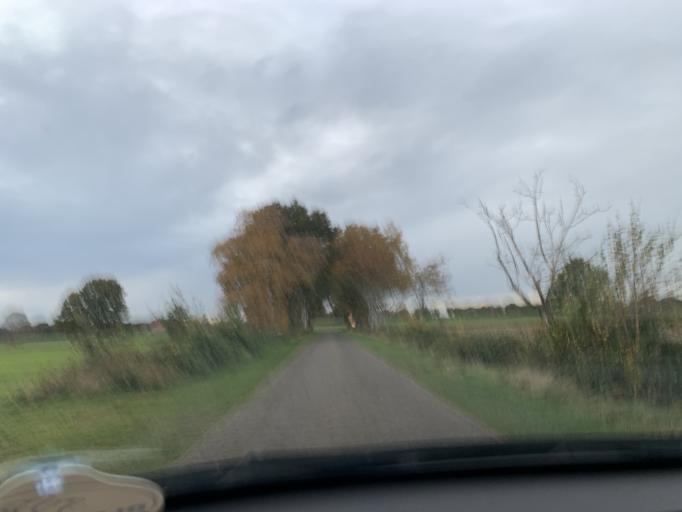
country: DE
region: Lower Saxony
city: Wiefelstede
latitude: 53.2684
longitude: 8.0480
